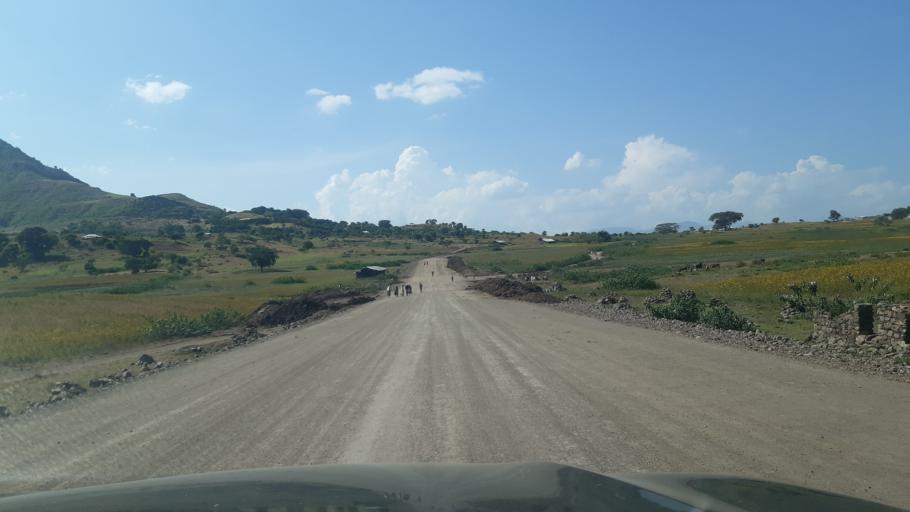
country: ET
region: Amhara
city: Dabat
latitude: 13.1574
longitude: 37.6114
